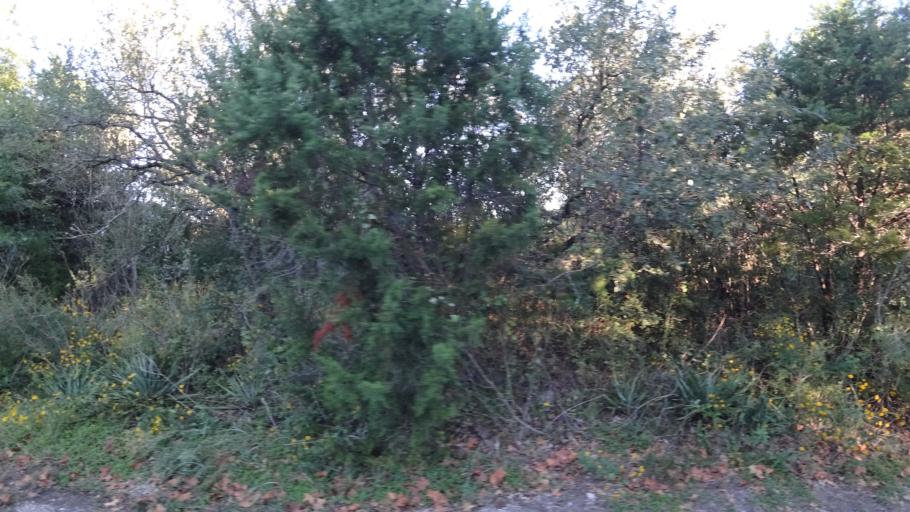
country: US
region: Texas
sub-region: Travis County
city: West Lake Hills
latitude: 30.3481
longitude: -97.8063
